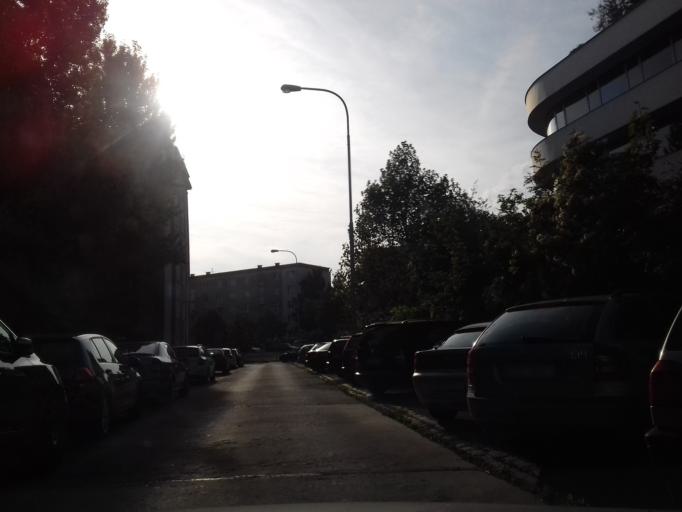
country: CZ
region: Praha
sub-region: Praha 4
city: Hodkovicky
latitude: 50.0445
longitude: 14.4438
